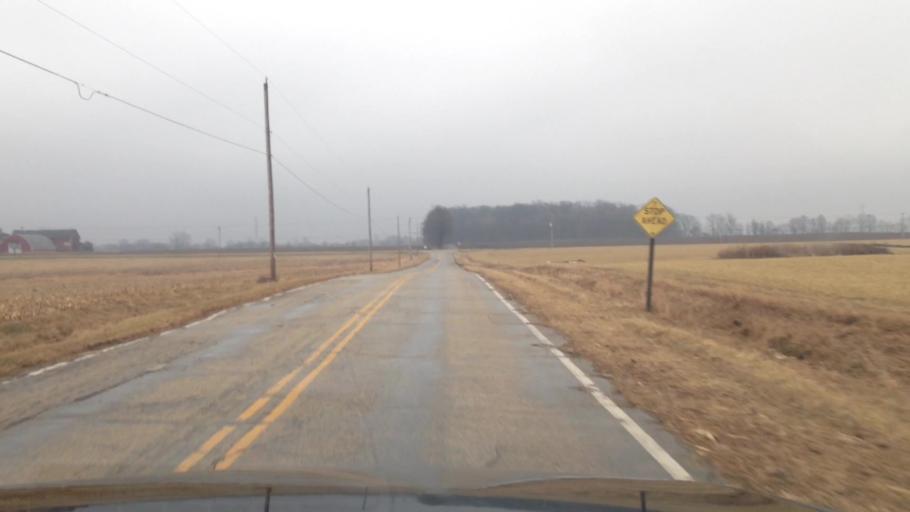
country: US
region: Wisconsin
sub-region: Washington County
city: Richfield
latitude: 43.2577
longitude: -88.1666
